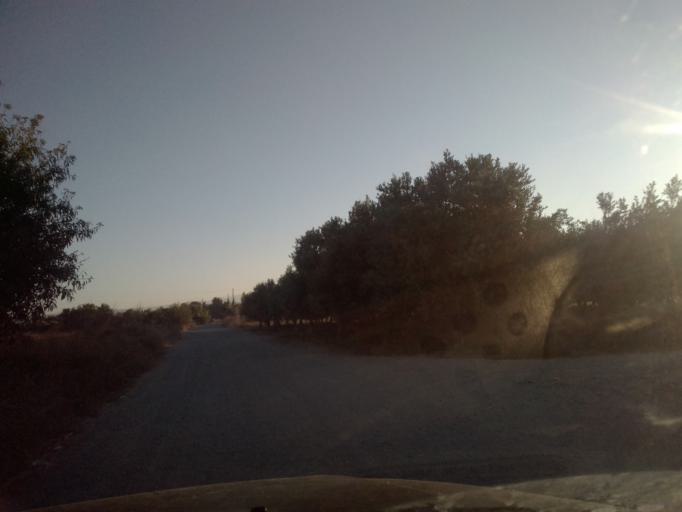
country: CY
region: Limassol
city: Ypsonas
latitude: 34.6642
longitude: 32.9681
